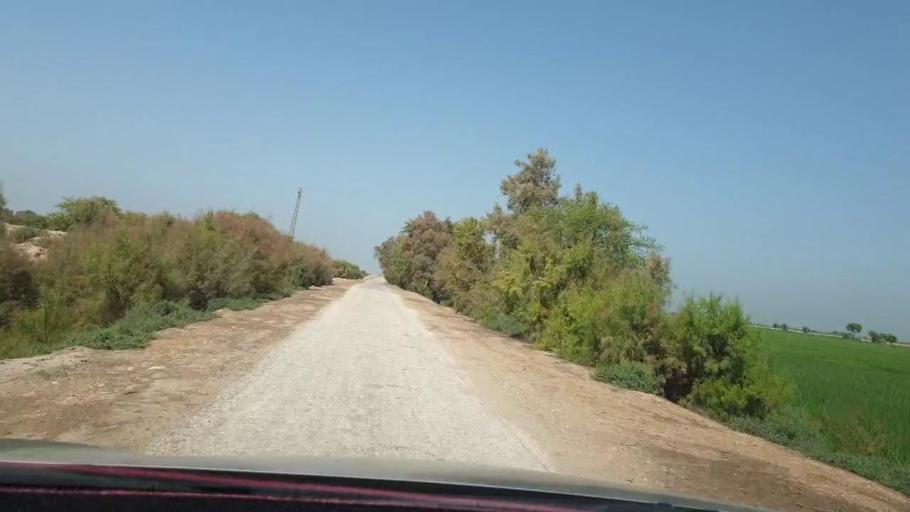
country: PK
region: Sindh
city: Warah
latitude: 27.5588
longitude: 67.7405
